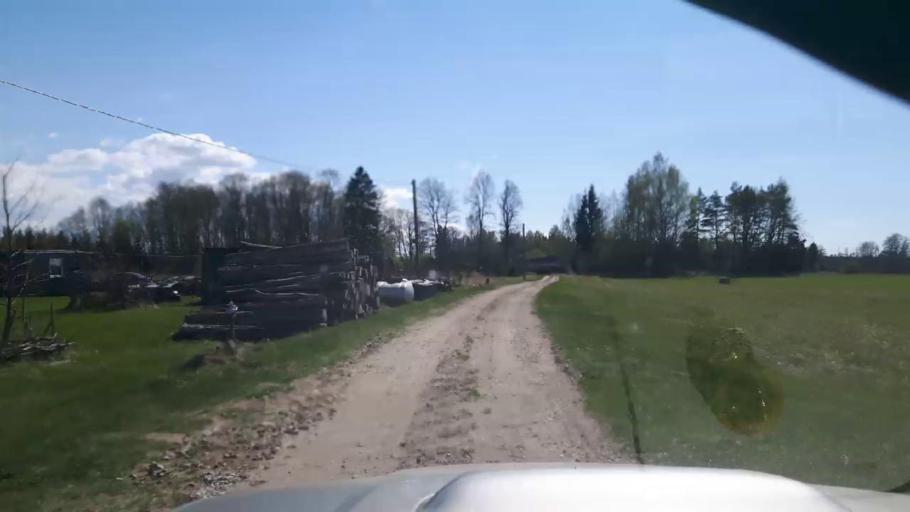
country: EE
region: Paernumaa
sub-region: Tootsi vald
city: Tootsi
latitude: 58.4642
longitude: 24.7989
